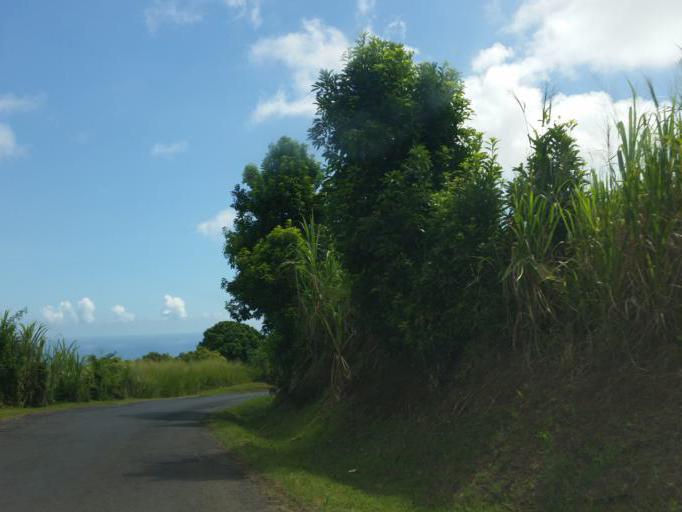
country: RE
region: Reunion
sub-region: Reunion
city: Sainte-Marie
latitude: -20.9332
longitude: 55.5289
